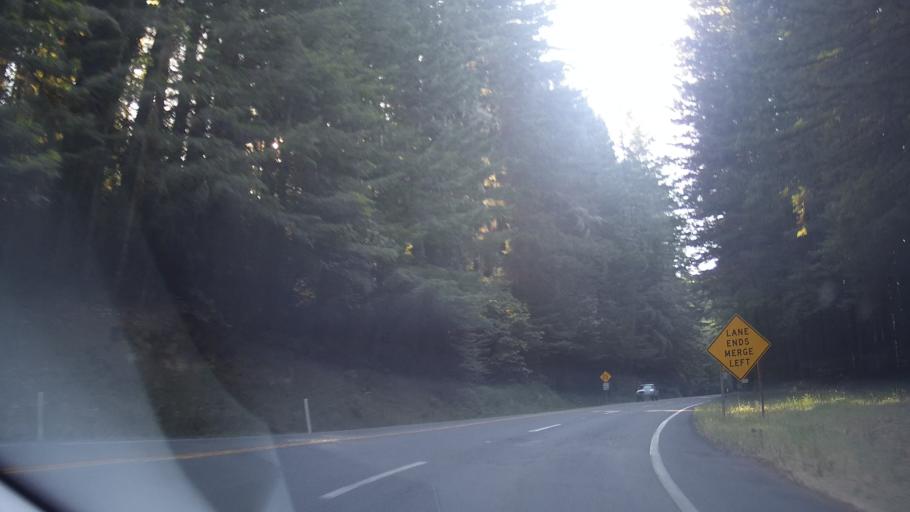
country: US
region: California
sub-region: Mendocino County
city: Fort Bragg
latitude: 39.3651
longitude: -123.6760
